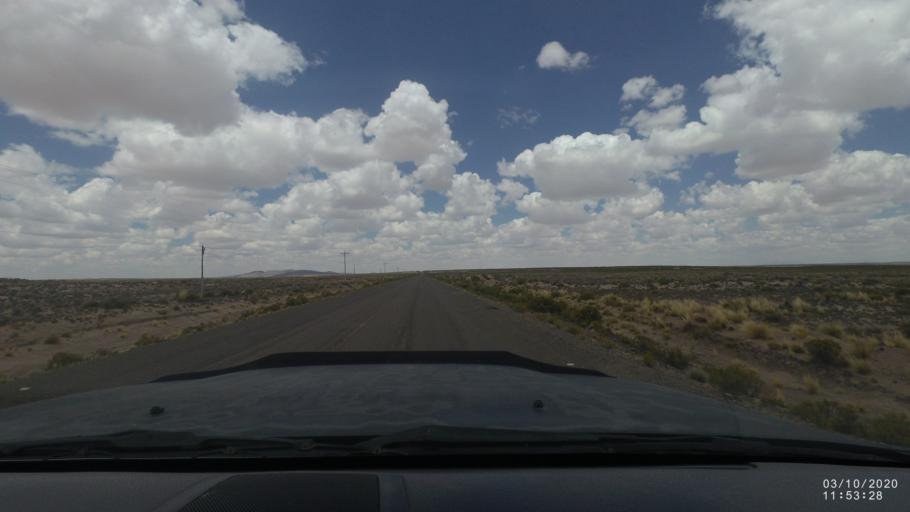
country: BO
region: Oruro
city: Poopo
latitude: -18.4791
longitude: -67.6043
